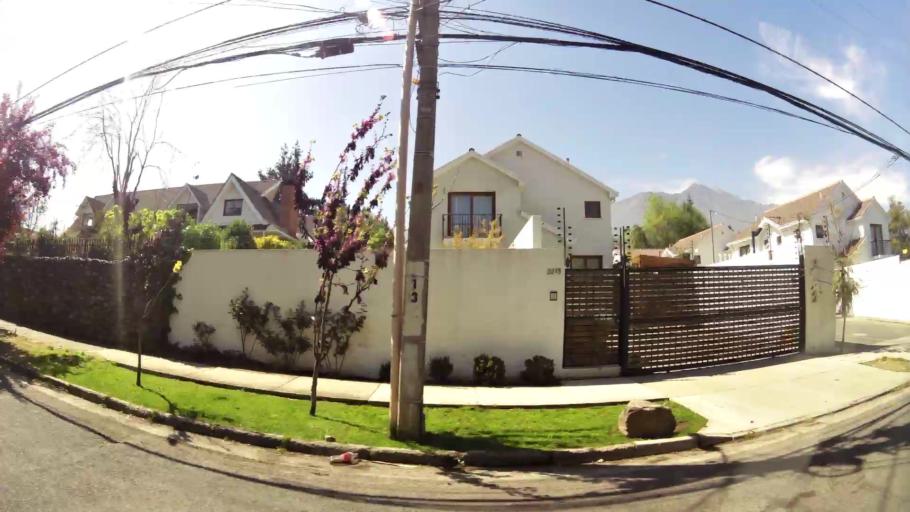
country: CL
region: Santiago Metropolitan
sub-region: Provincia de Santiago
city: Villa Presidente Frei, Nunoa, Santiago, Chile
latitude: -33.4368
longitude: -70.5297
